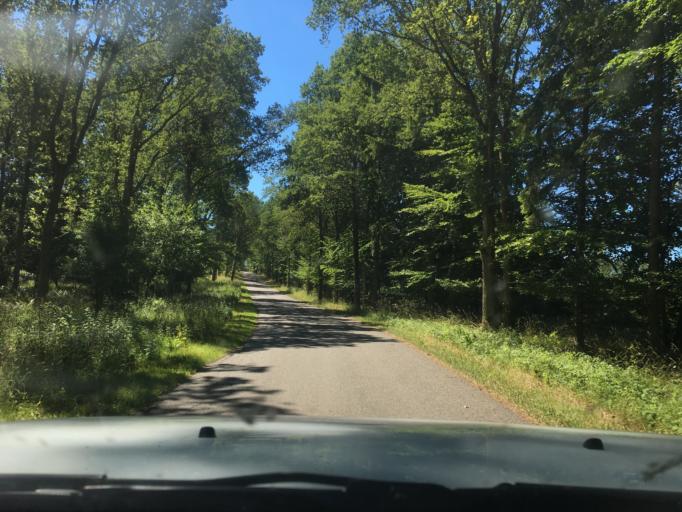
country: DK
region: Central Jutland
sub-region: Norddjurs Kommune
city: Auning
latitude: 56.3599
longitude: 10.3918
